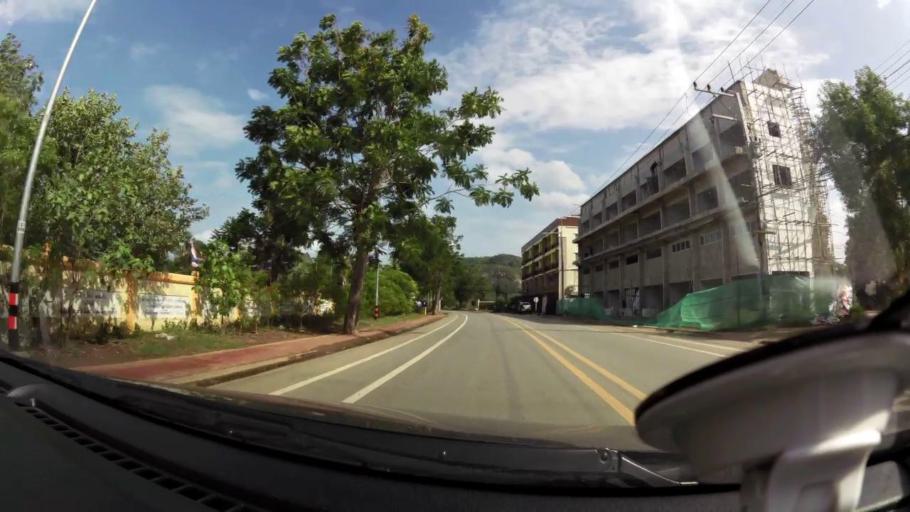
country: TH
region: Prachuap Khiri Khan
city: Pran Buri
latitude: 12.4623
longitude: 99.9745
